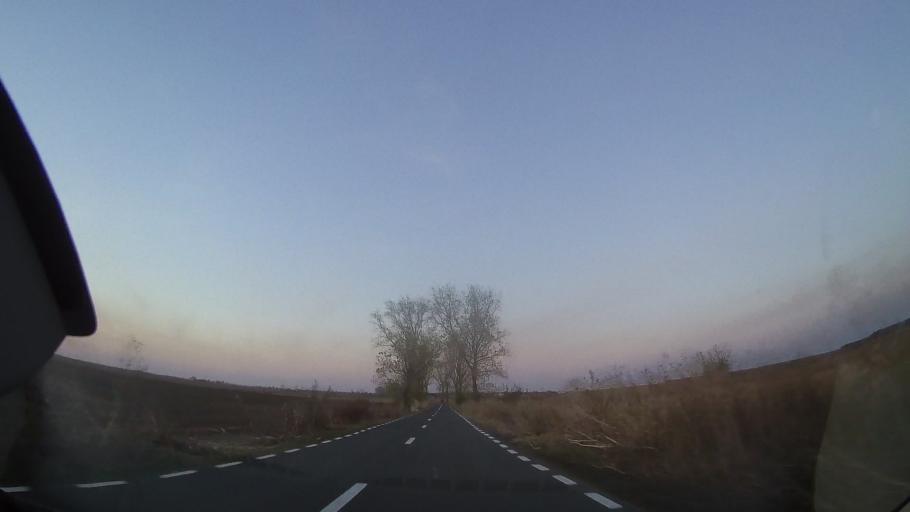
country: RO
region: Constanta
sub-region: Comuna Cobadin
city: Cobadin
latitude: 44.0379
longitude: 28.2583
